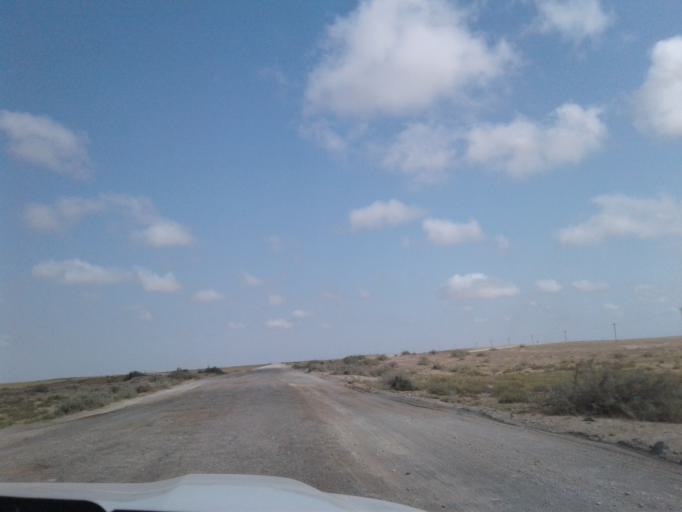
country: IR
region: Golestan
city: Gomishan
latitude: 37.6480
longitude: 53.9314
